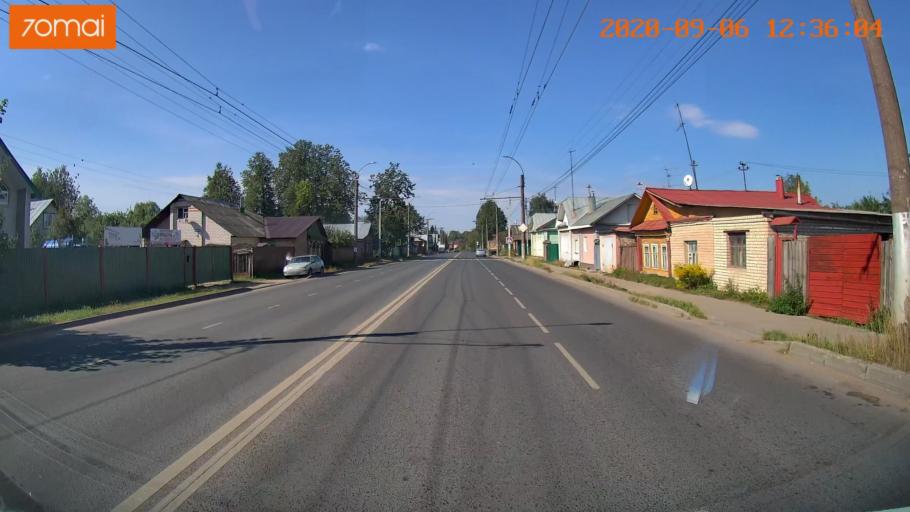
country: RU
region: Ivanovo
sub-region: Gorod Ivanovo
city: Ivanovo
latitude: 57.0215
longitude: 40.9886
